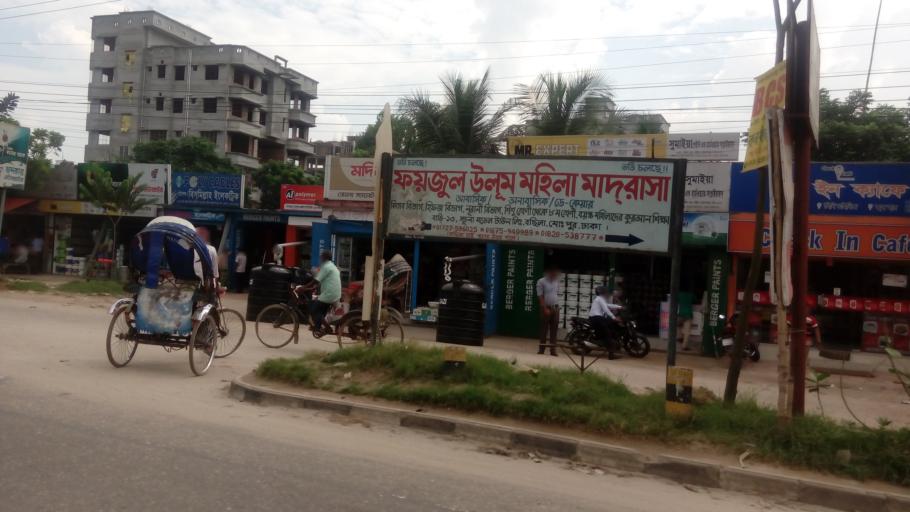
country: BD
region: Dhaka
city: Azimpur
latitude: 23.7457
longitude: 90.3493
